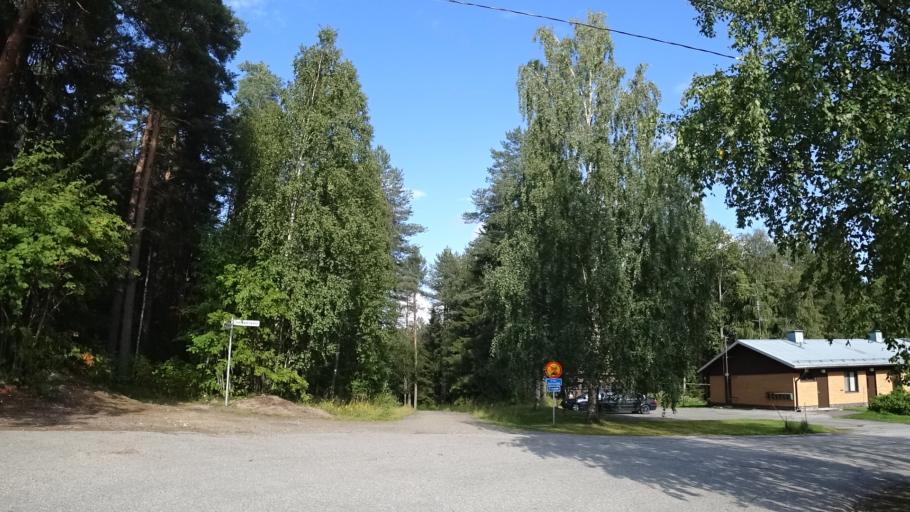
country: FI
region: North Karelia
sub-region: Pielisen Karjala
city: Lieksa
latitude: 63.3349
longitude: 30.0329
